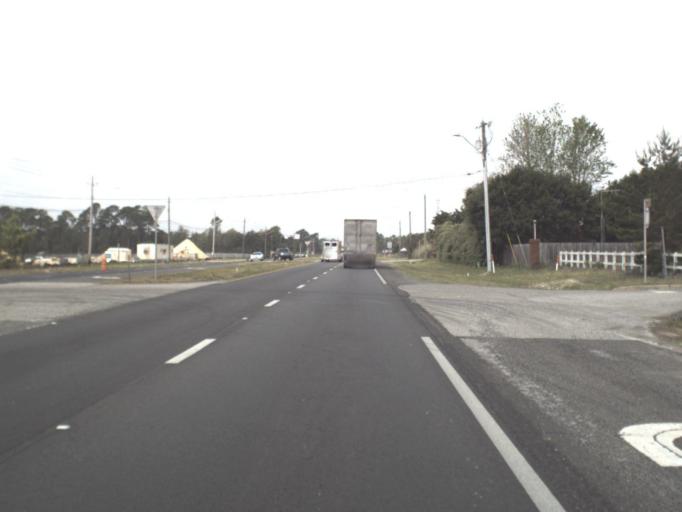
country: US
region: Florida
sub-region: Santa Rosa County
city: Holley
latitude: 30.4021
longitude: -86.9117
